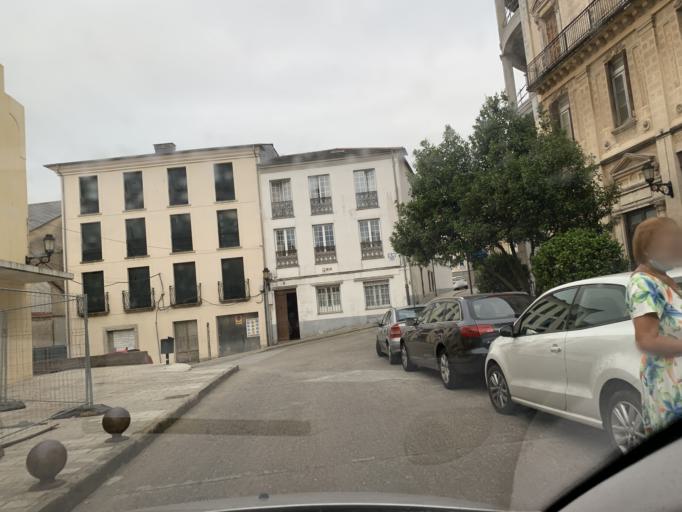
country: ES
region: Galicia
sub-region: Provincia de Lugo
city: Ribadeo
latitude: 43.5369
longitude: -7.0396
